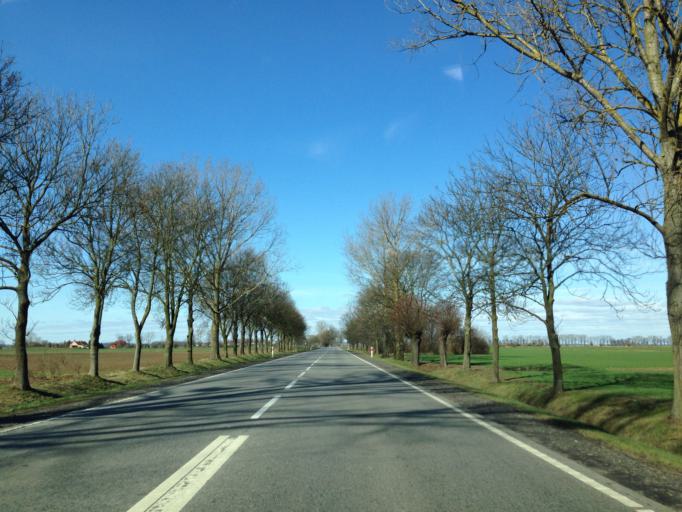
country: PL
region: Pomeranian Voivodeship
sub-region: Powiat malborski
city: Miloradz
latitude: 54.0499
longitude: 18.9410
